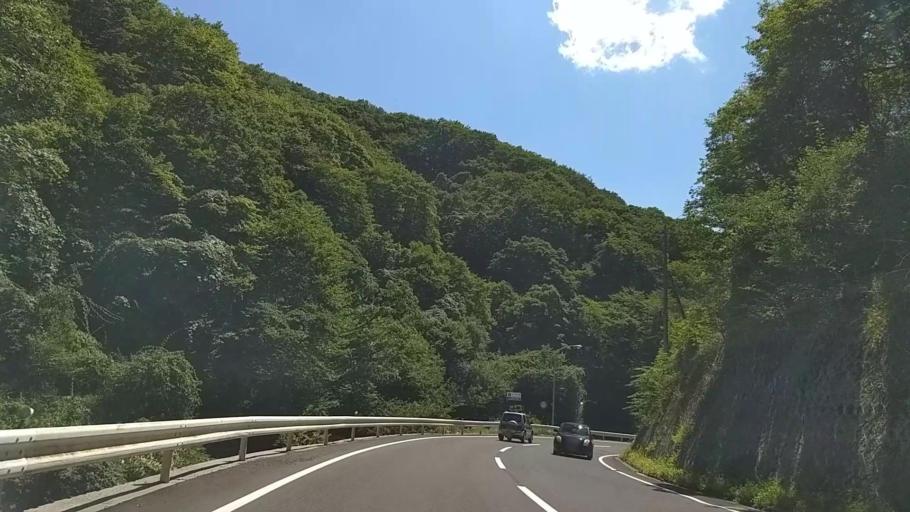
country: JP
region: Nagano
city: Chino
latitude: 36.0945
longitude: 138.2239
